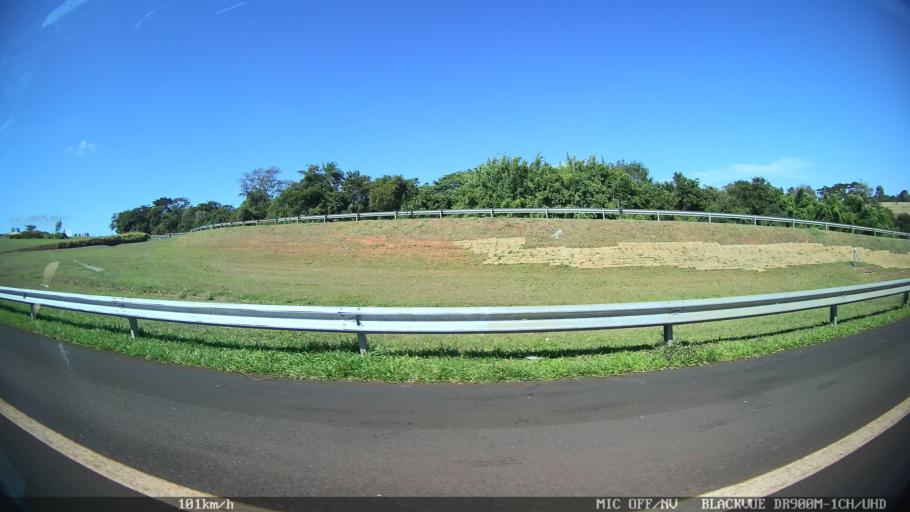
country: BR
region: Sao Paulo
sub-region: Franca
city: Franca
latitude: -20.5627
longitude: -47.4152
